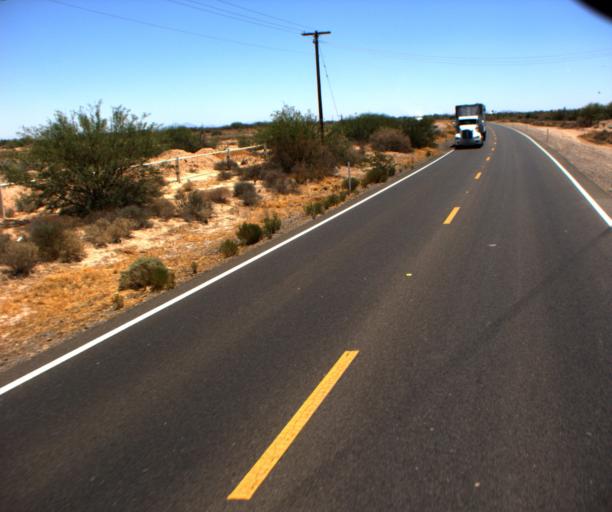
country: US
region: Arizona
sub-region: Pinal County
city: Maricopa
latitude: 33.0727
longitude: -112.0790
